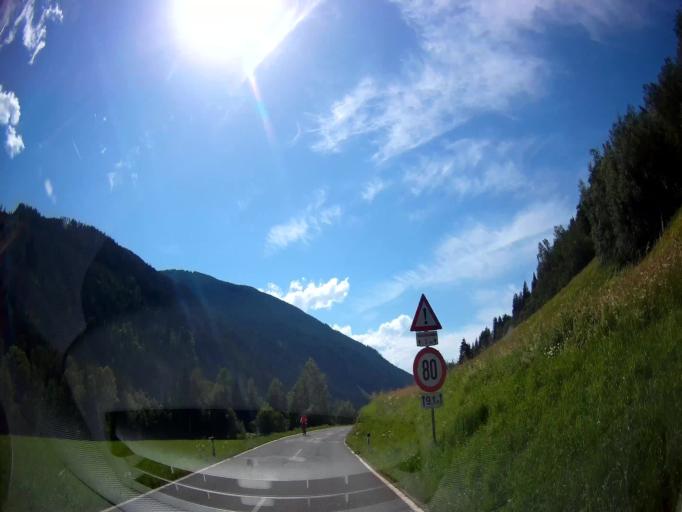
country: AT
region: Salzburg
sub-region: Politischer Bezirk Tamsweg
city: Thomatal
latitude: 47.0635
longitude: 13.7766
